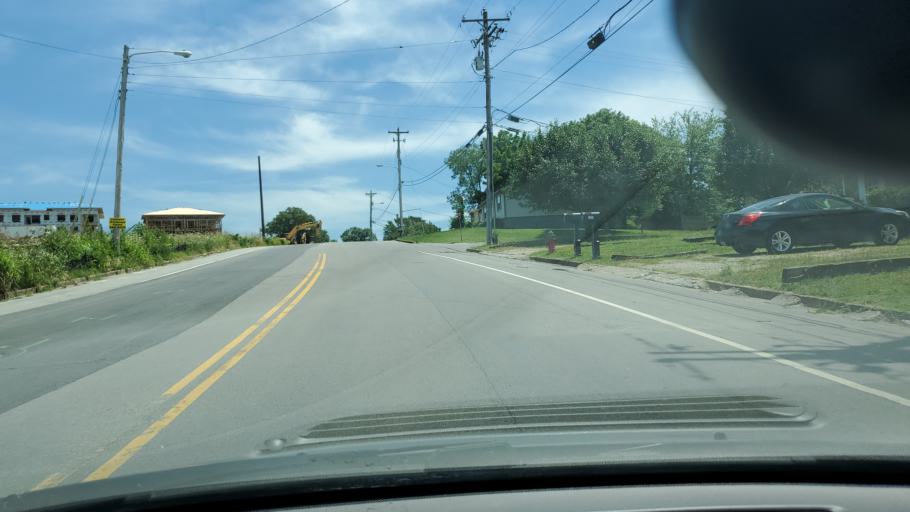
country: US
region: Tennessee
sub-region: Davidson County
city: Nashville
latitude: 36.2095
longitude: -86.7533
